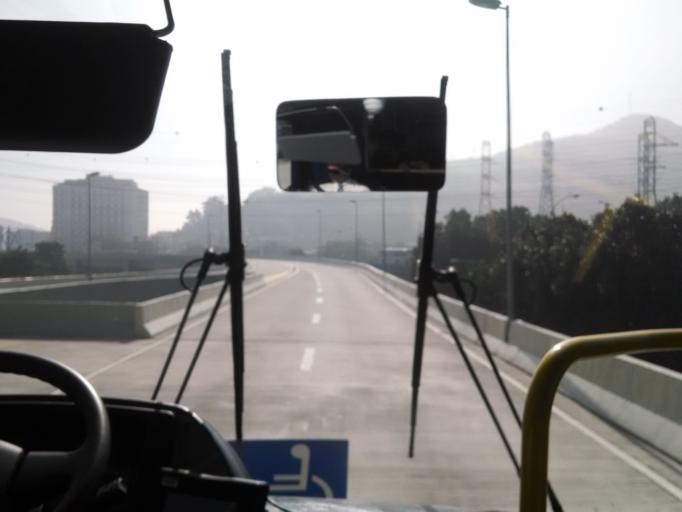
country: BR
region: Rio de Janeiro
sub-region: Sao Joao De Meriti
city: Sao Joao de Meriti
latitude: -22.8766
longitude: -43.3356
